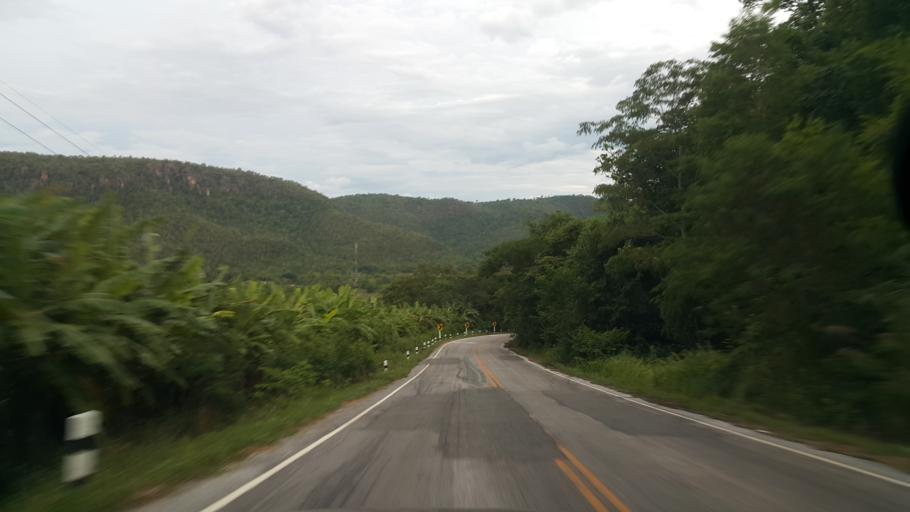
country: TH
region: Loei
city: Na Haeo
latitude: 17.4928
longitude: 101.1754
